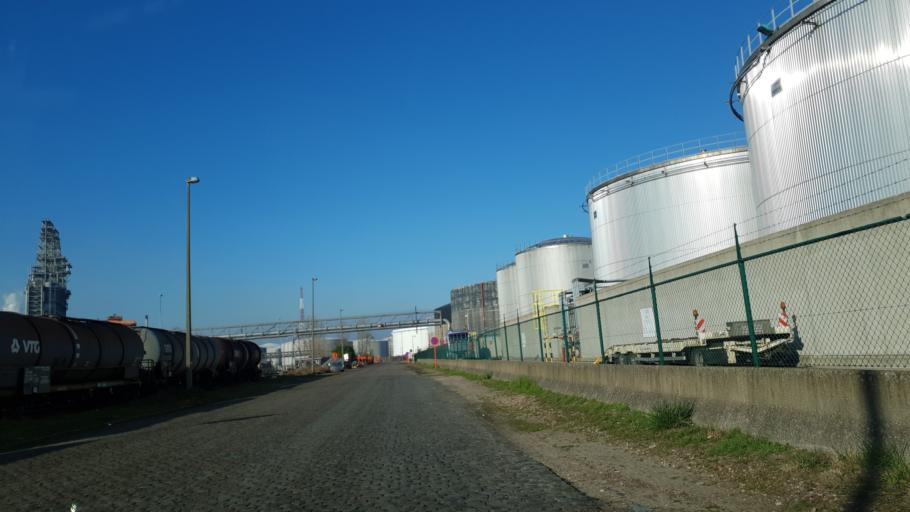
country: BE
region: Flanders
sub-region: Provincie Antwerpen
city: Zwijndrecht
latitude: 51.2627
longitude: 4.3442
